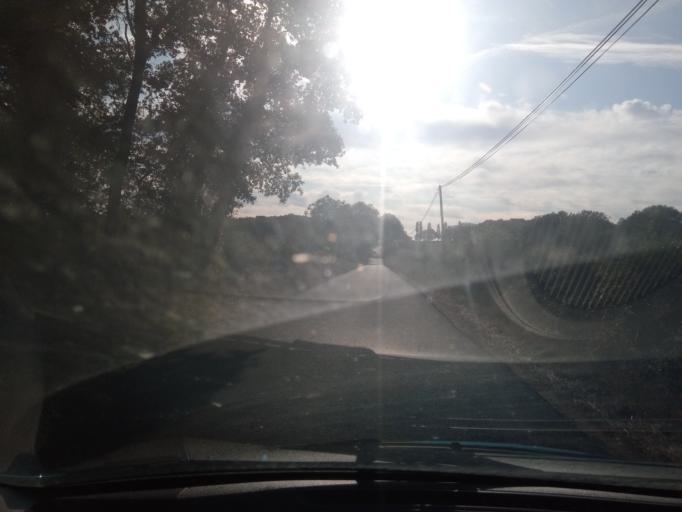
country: FR
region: Poitou-Charentes
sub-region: Departement de la Vienne
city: Montmorillon
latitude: 46.4956
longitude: 0.8268
